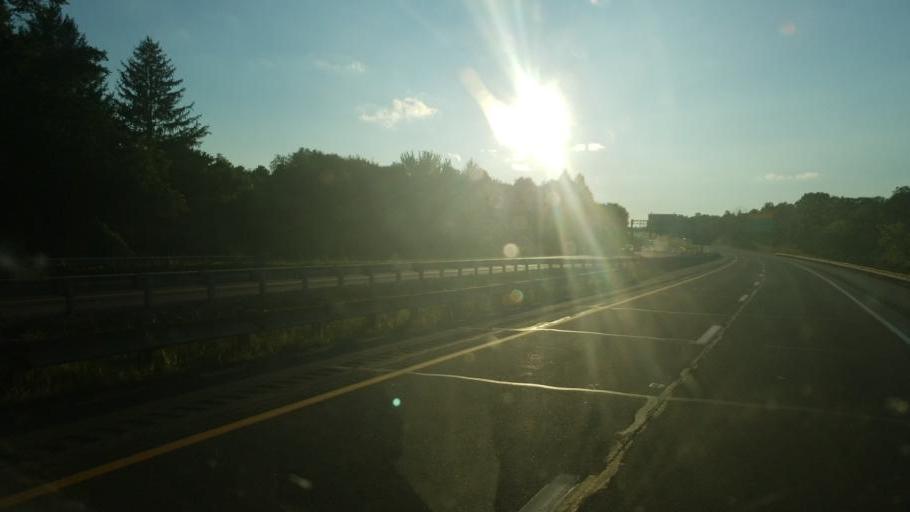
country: US
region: Ohio
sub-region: Mahoning County
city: New Middletown
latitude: 40.9155
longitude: -80.5260
